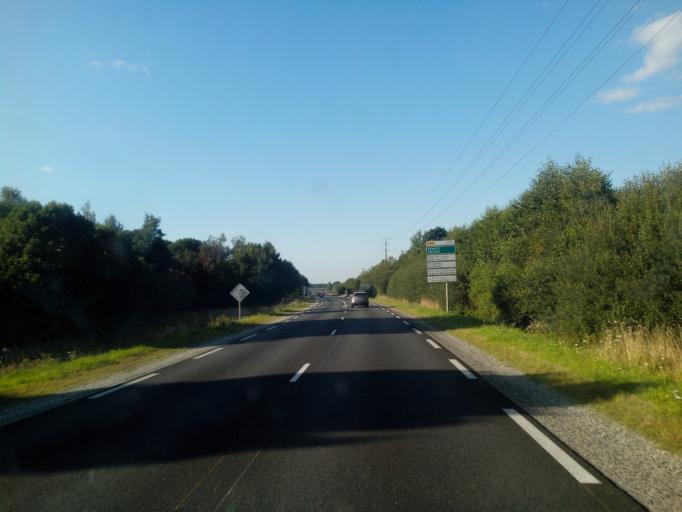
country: FR
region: Brittany
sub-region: Departement du Morbihan
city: Saint-Thuriau
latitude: 48.0488
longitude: -2.9452
